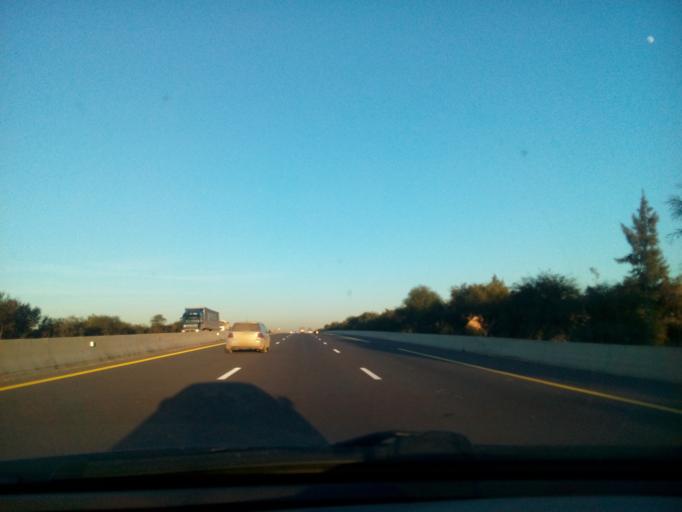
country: DZ
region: Relizane
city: Oued Rhiou
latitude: 35.9966
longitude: 0.9907
